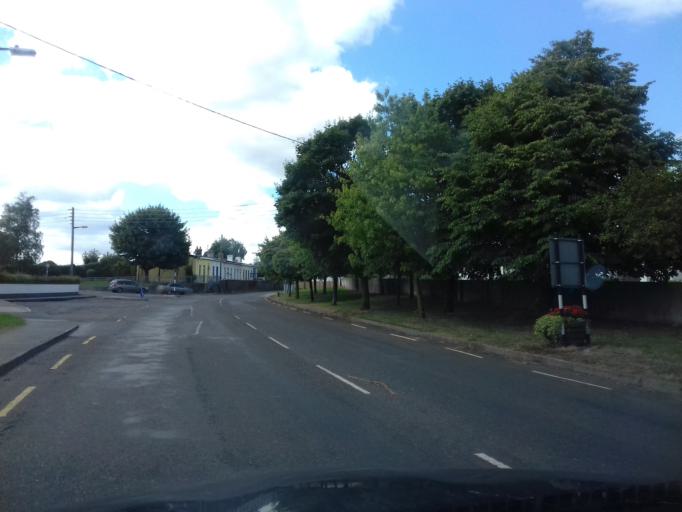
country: IE
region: Munster
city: Carrick-on-Suir
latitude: 52.3517
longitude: -7.4188
